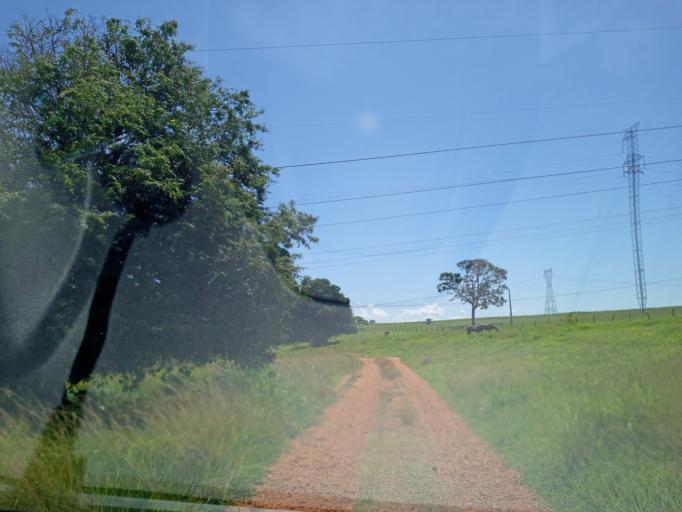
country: BR
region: Goias
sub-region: Itumbiara
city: Itumbiara
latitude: -18.3986
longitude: -49.1265
